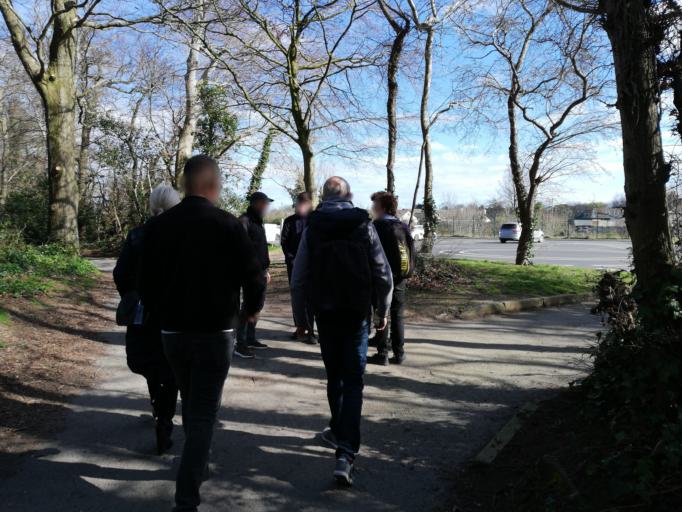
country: IE
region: Leinster
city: Malahide
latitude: 53.4428
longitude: -6.1578
